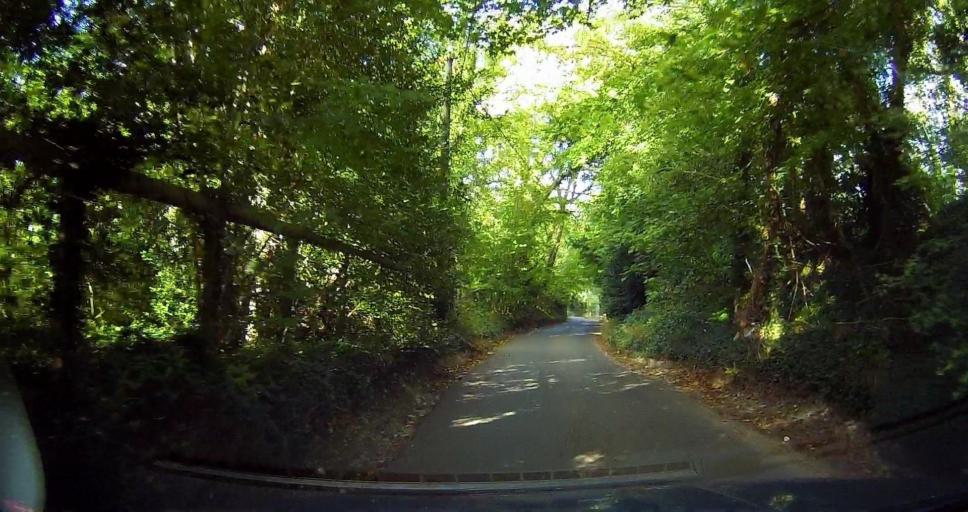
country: GB
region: England
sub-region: Kent
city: Longfield
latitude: 51.3596
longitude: 0.2721
